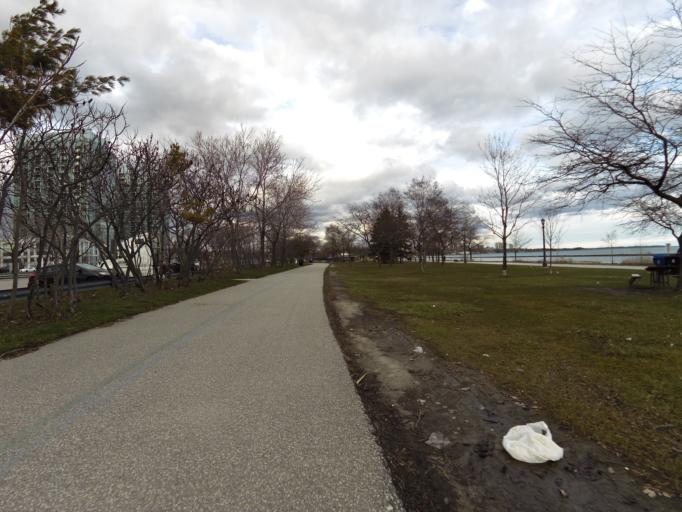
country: CA
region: Ontario
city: Toronto
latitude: 43.6347
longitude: -79.4677
